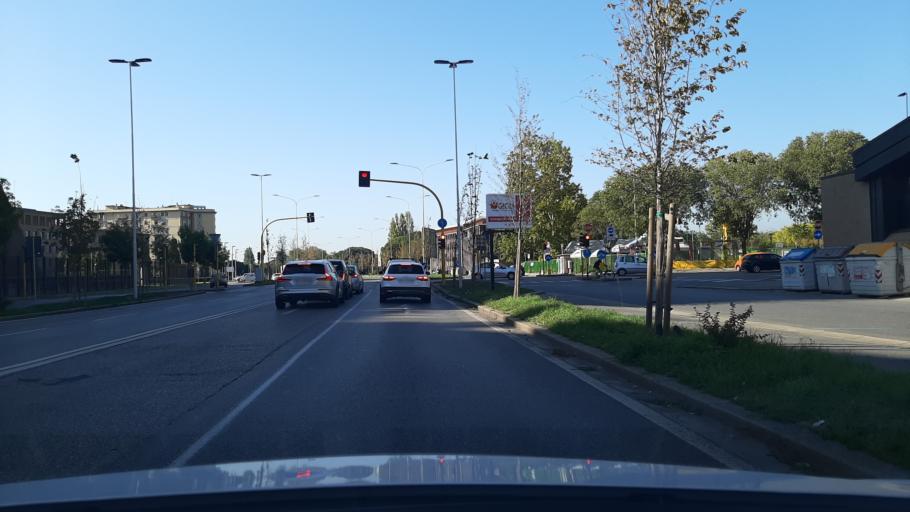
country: IT
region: Tuscany
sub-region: Province of Florence
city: Florence
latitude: 43.7964
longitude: 11.2261
